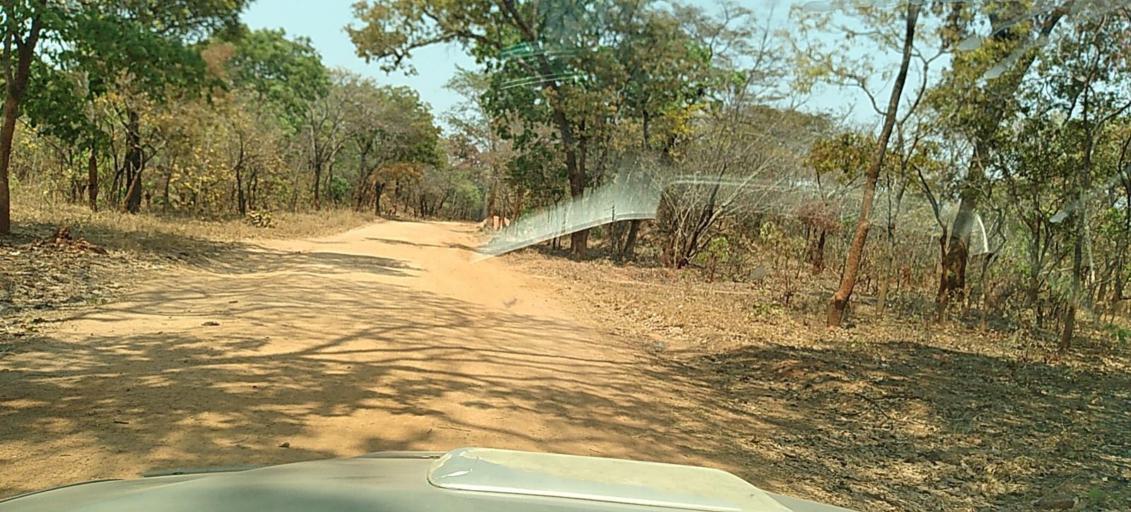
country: ZM
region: North-Western
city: Kasempa
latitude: -13.6691
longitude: 26.2946
